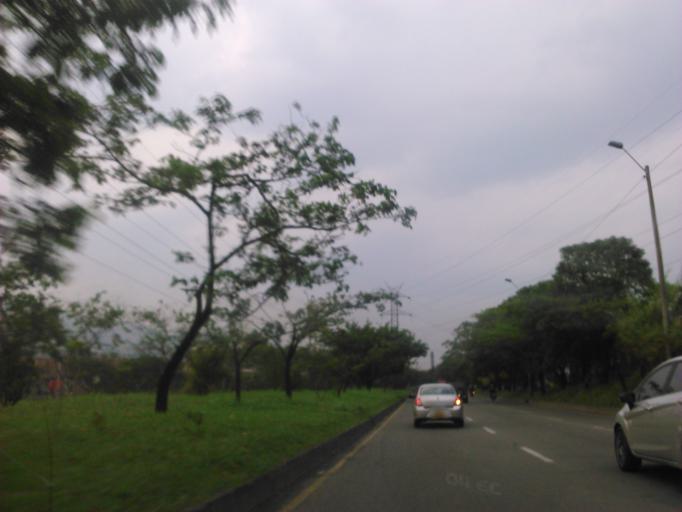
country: CO
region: Antioquia
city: Envigado
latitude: 6.1665
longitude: -75.6027
